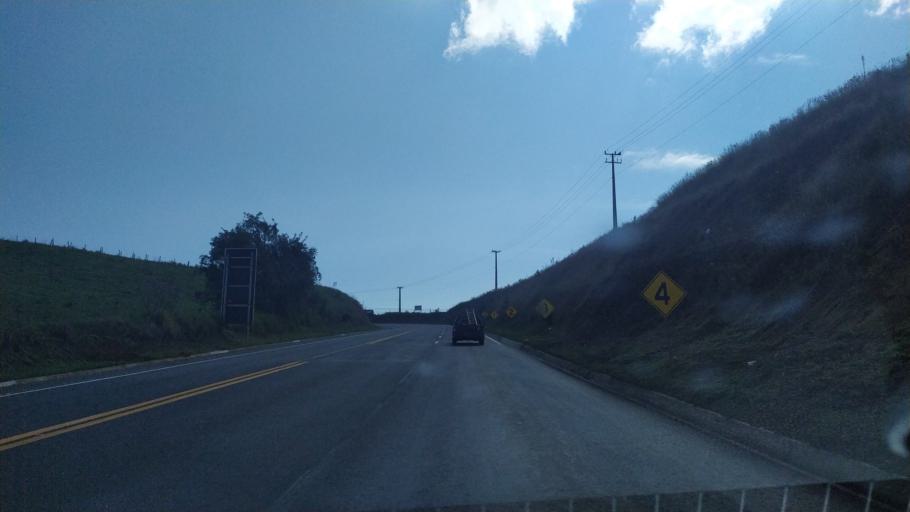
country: BR
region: Parana
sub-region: Telemaco Borba
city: Telemaco Borba
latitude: -24.2866
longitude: -50.7049
